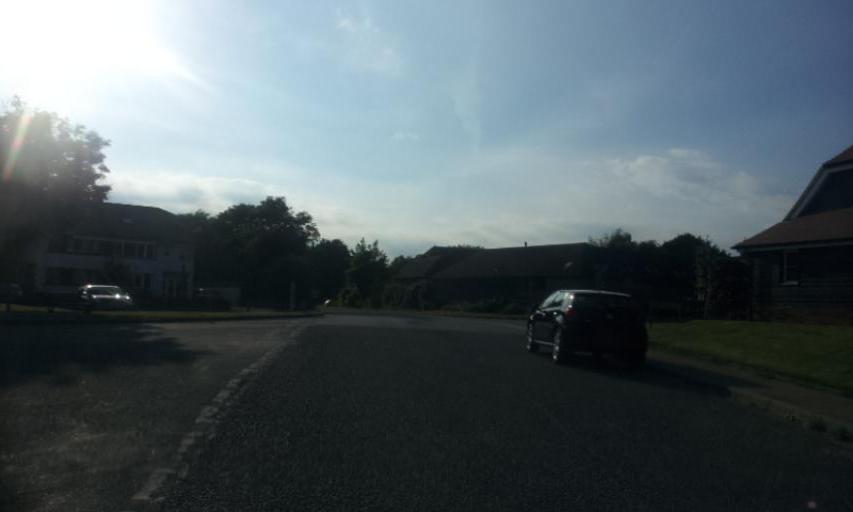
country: GB
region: England
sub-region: Kent
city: Boxley
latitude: 51.3050
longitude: 0.5148
